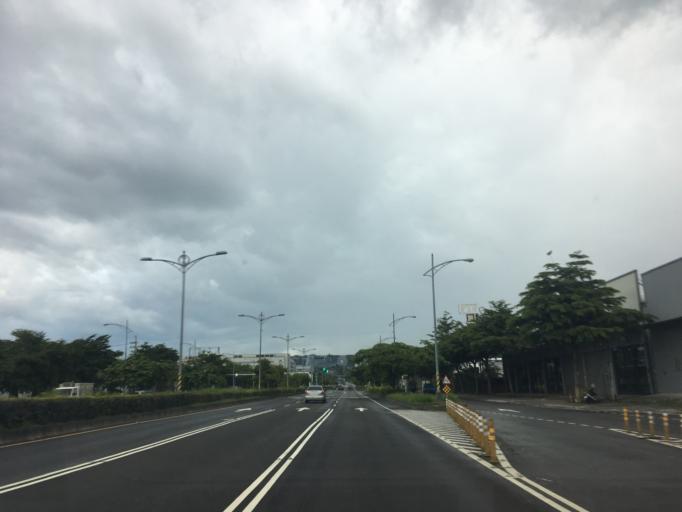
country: TW
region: Taiwan
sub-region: Taichung City
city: Taichung
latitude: 24.2043
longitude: 120.6349
